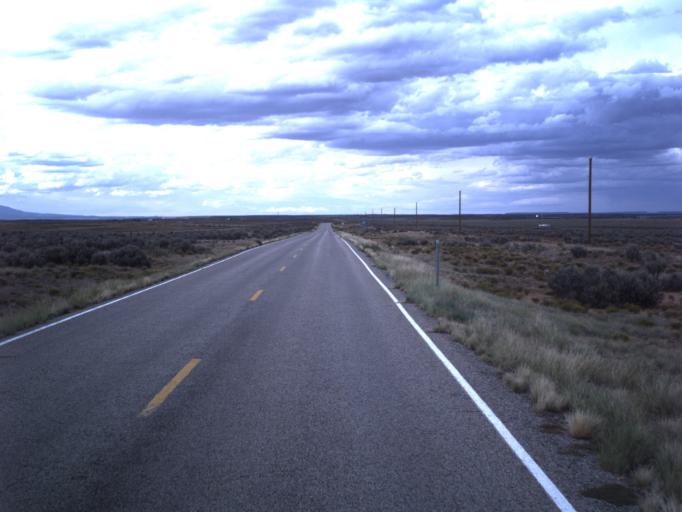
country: US
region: Utah
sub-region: San Juan County
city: Blanding
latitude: 37.4104
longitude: -109.3356
